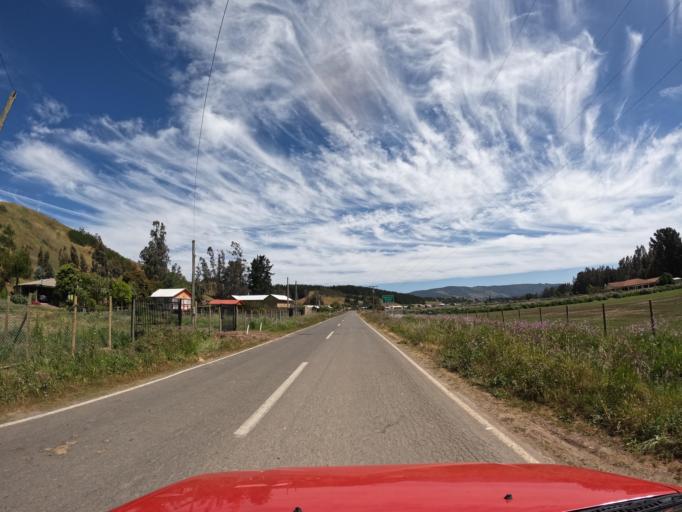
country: CL
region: Maule
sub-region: Provincia de Talca
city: Constitucion
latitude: -35.0184
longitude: -72.0390
